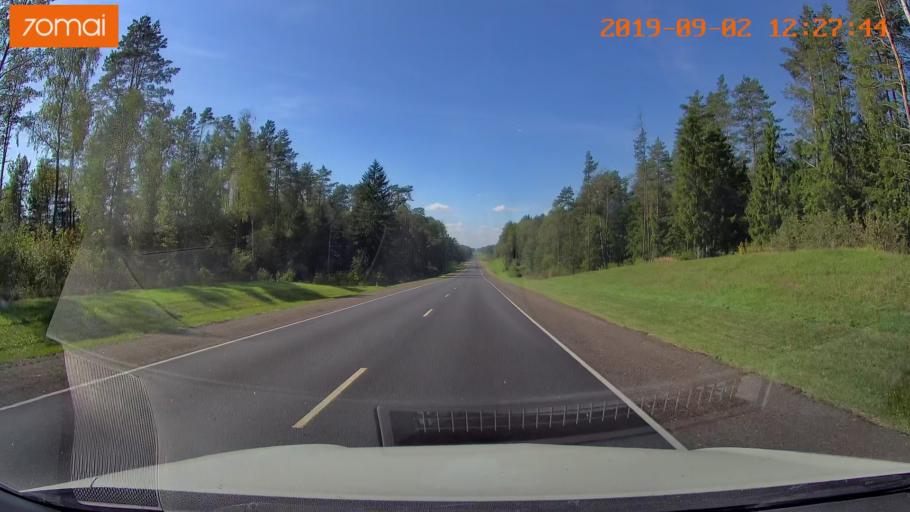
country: RU
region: Smolensk
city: Shumyachi
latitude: 53.8513
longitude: 32.5367
